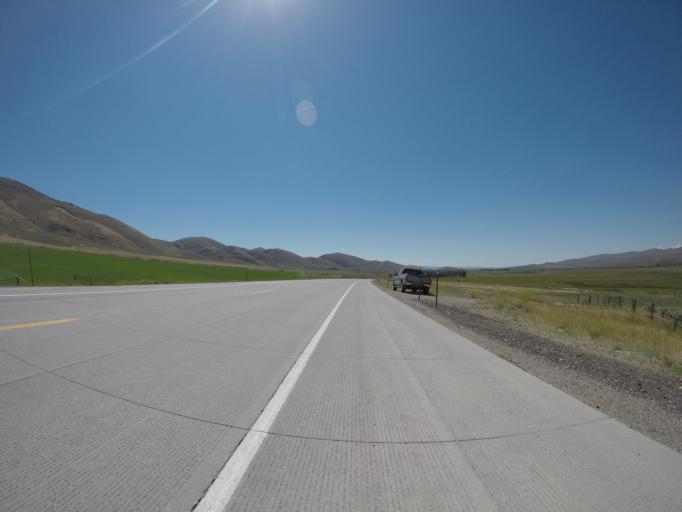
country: US
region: Idaho
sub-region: Bear Lake County
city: Montpelier
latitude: 42.1726
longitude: -110.9944
